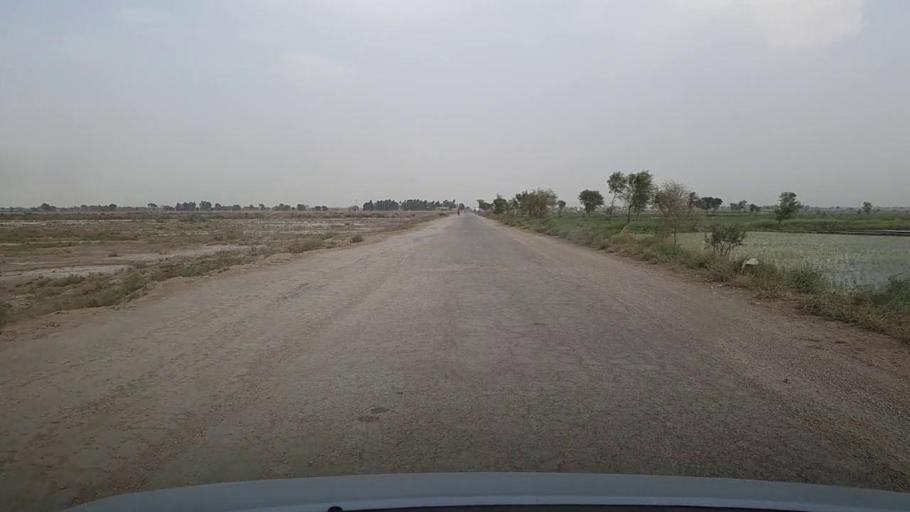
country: PK
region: Sindh
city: Dadu
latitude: 26.8141
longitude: 67.7731
